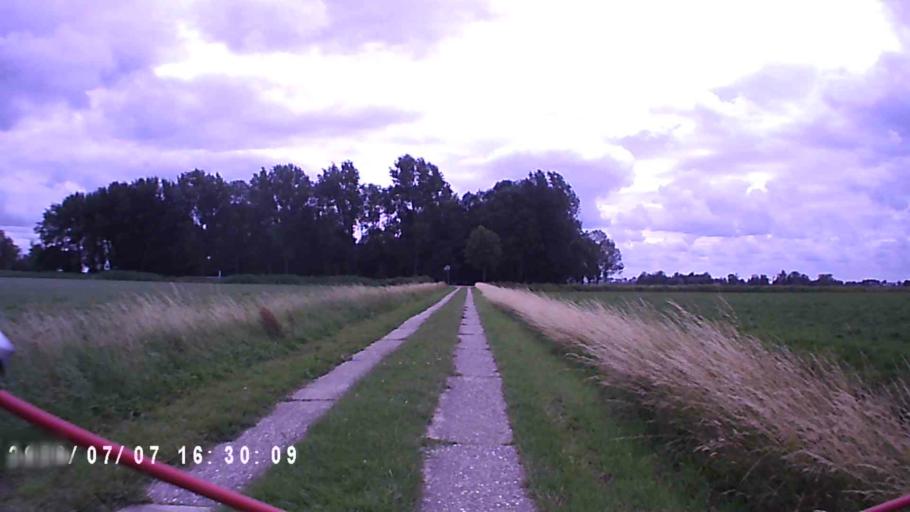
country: NL
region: Groningen
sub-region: Gemeente Winsum
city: Winsum
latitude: 53.3570
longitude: 6.5486
